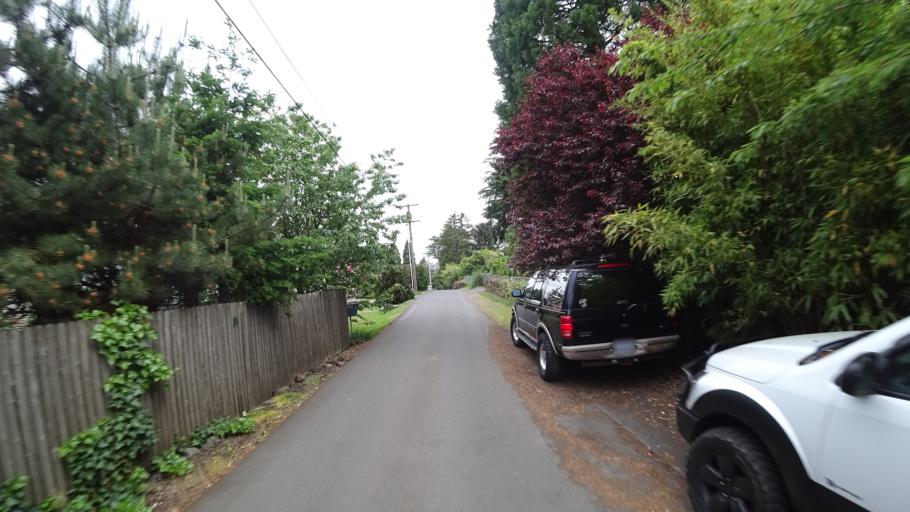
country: US
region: Oregon
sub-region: Washington County
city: Garden Home-Whitford
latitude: 45.4655
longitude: -122.7361
